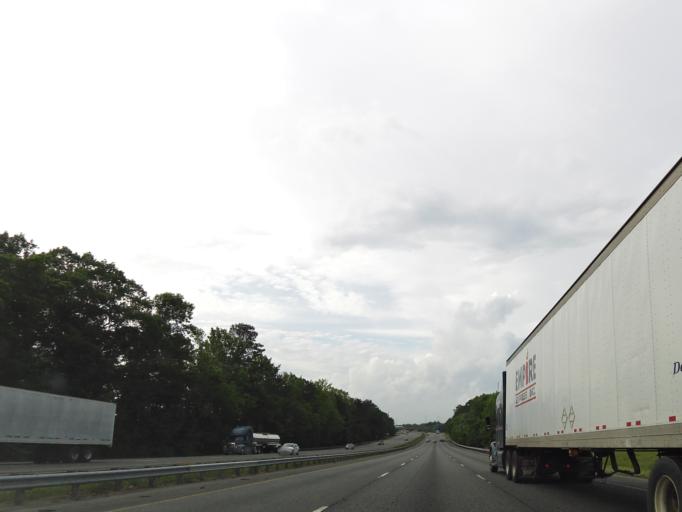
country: US
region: Georgia
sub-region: Butts County
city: Jackson
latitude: 33.1983
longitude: -84.0591
